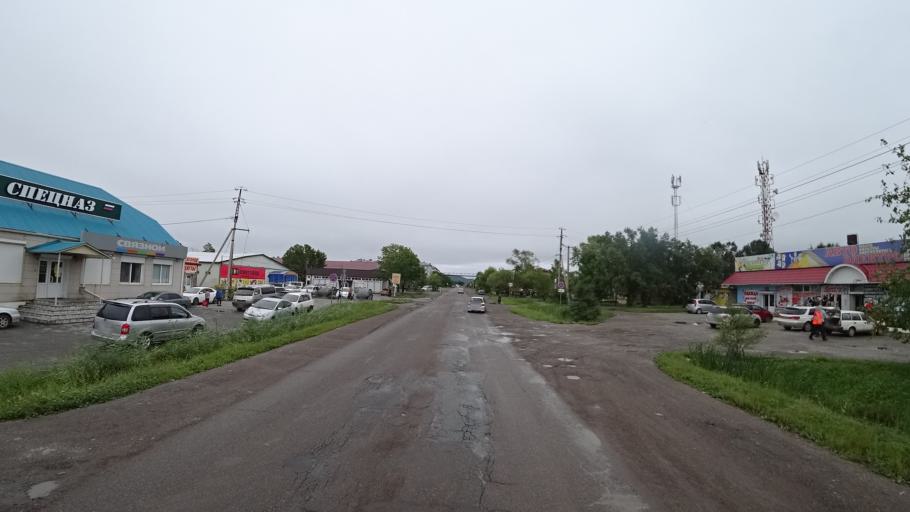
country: RU
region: Primorskiy
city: Monastyrishche
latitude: 44.2055
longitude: 132.4428
